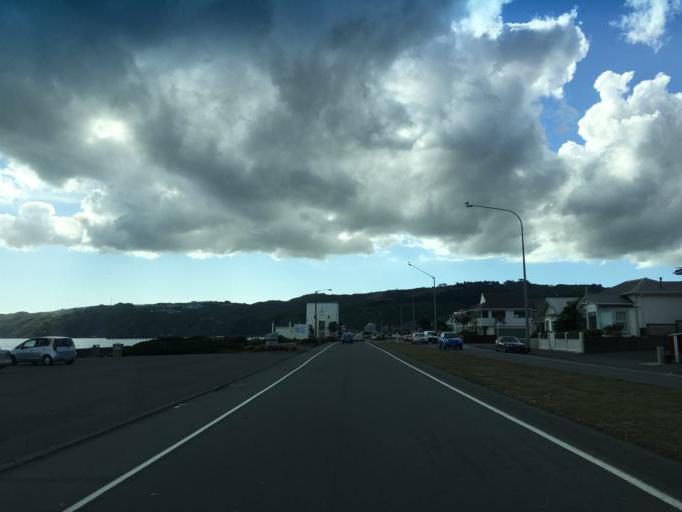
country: NZ
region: Wellington
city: Petone
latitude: -41.2298
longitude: 174.8823
